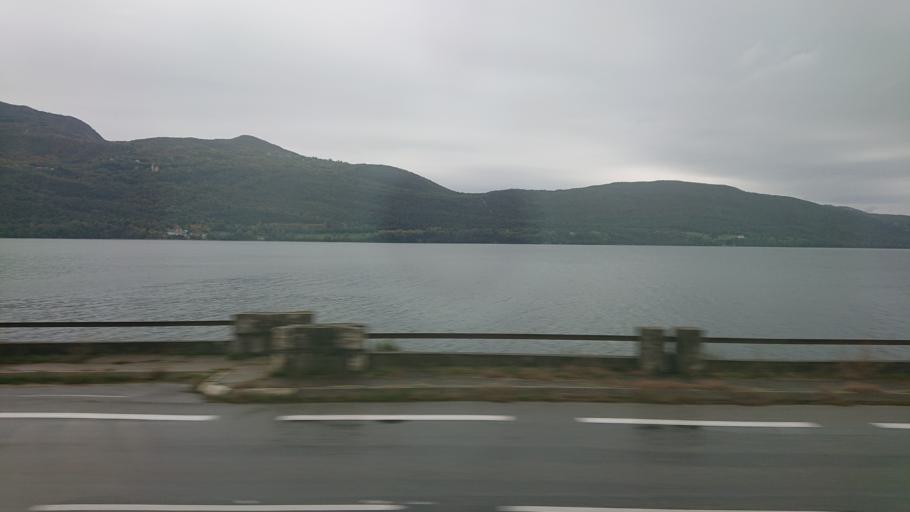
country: FR
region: Rhone-Alpes
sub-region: Departement de la Savoie
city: Brison-Saint-Innocent
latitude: 45.7634
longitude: 5.8703
